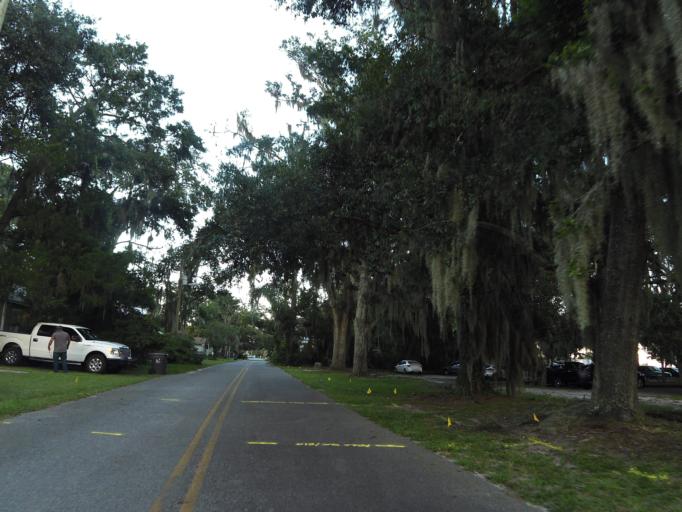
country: US
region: Georgia
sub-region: Camden County
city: St. Marys
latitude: 30.7216
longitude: -81.5514
